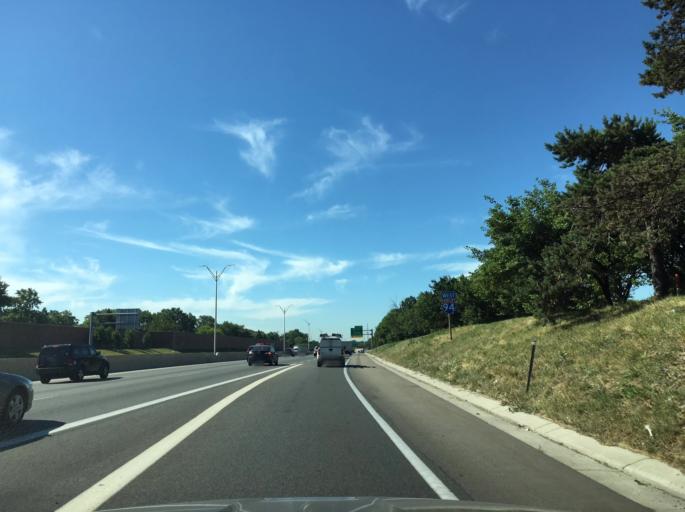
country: US
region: Michigan
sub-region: Macomb County
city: Roseville
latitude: 42.5070
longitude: -82.9184
